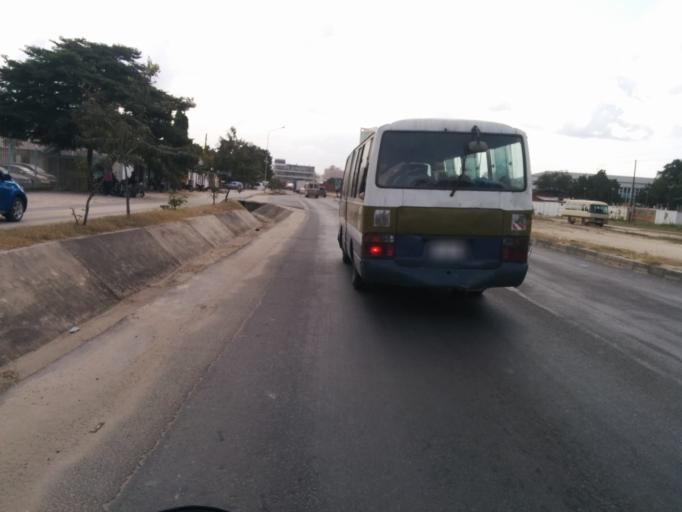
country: TZ
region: Dar es Salaam
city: Dar es Salaam
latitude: -6.8331
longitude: 39.2865
